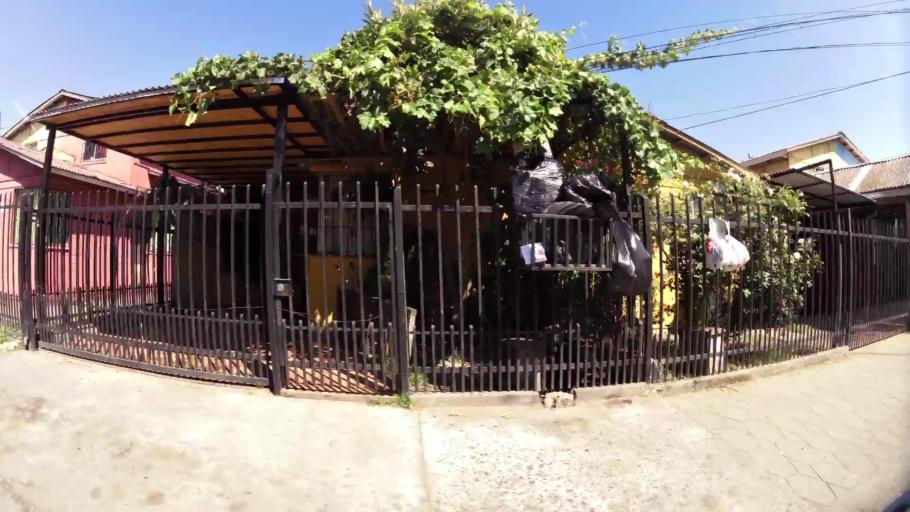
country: CL
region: Maule
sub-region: Provincia de Curico
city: Curico
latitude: -34.9666
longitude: -71.2466
